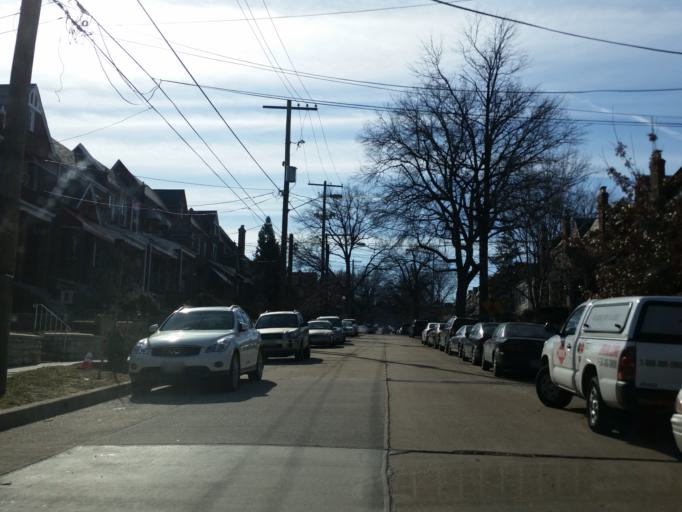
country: US
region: Maryland
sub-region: Montgomery County
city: Takoma Park
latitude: 38.9520
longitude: -77.0159
